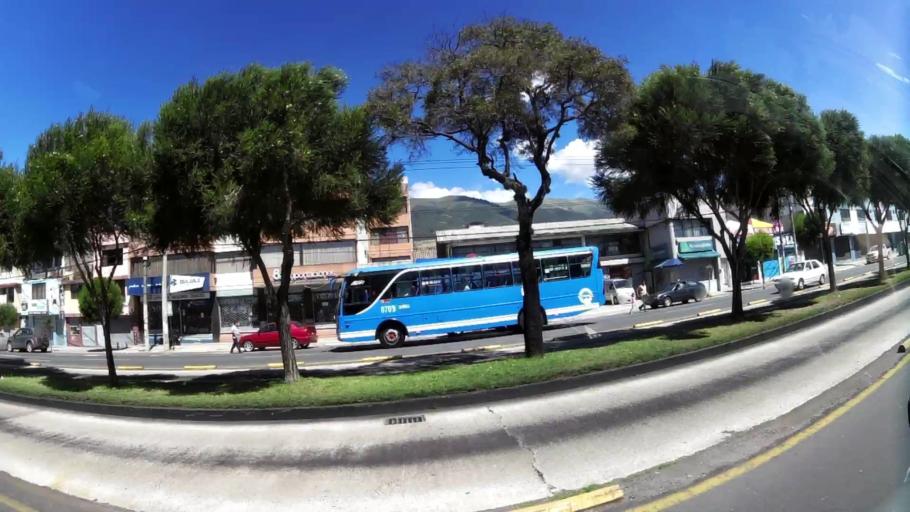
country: EC
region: Pichincha
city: Quito
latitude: -0.1552
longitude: -78.4889
